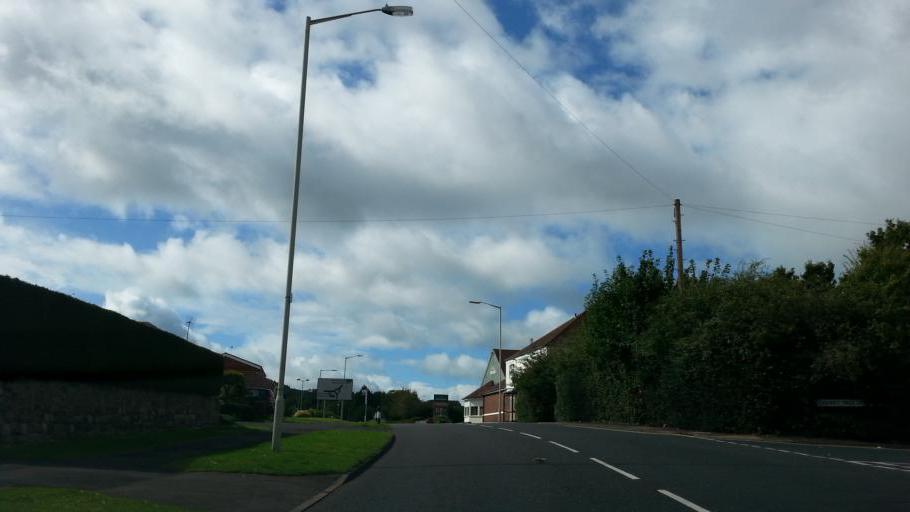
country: GB
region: England
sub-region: Dudley
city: Halesowen
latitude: 52.4385
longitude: -2.0754
